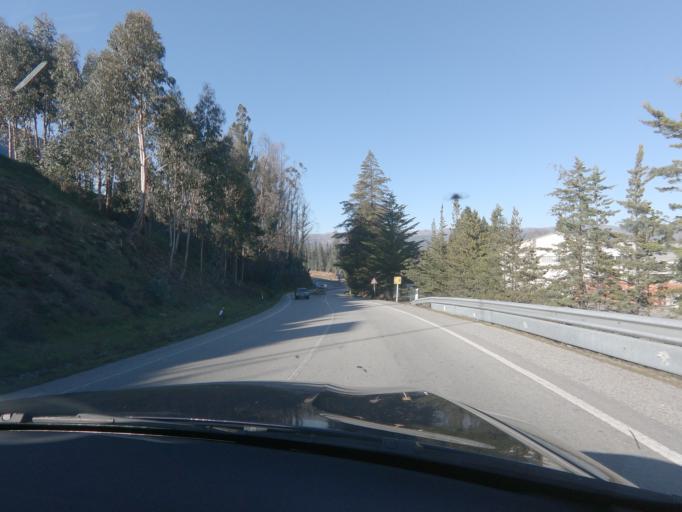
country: PT
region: Viseu
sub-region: Vouzela
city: Vouzela
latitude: 40.7268
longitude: -8.1251
